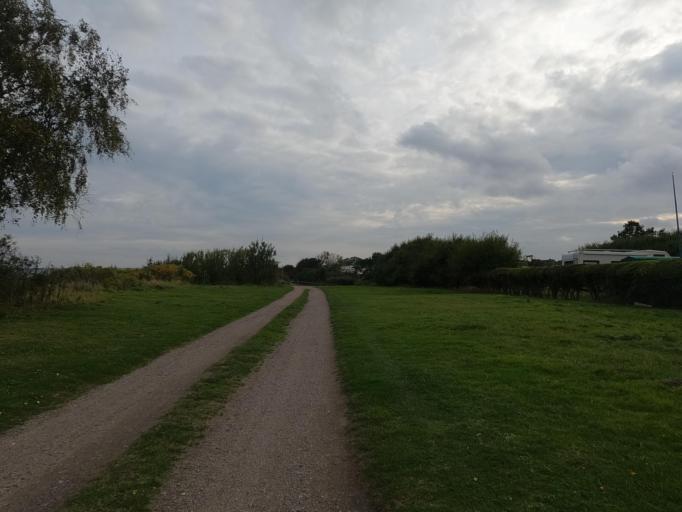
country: DE
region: Schleswig-Holstein
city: Grossenbrode
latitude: 54.3299
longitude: 11.0722
